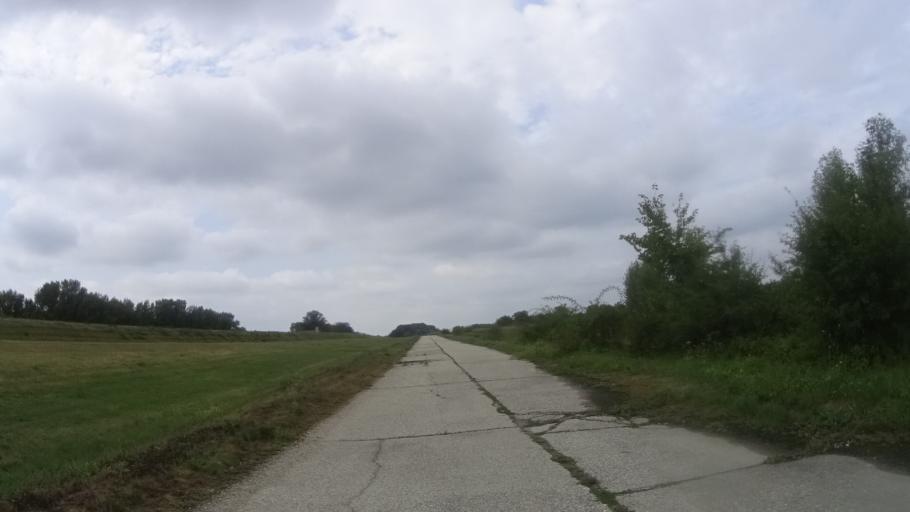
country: HU
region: Komarom-Esztergom
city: Acs
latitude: 47.7547
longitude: 17.9232
